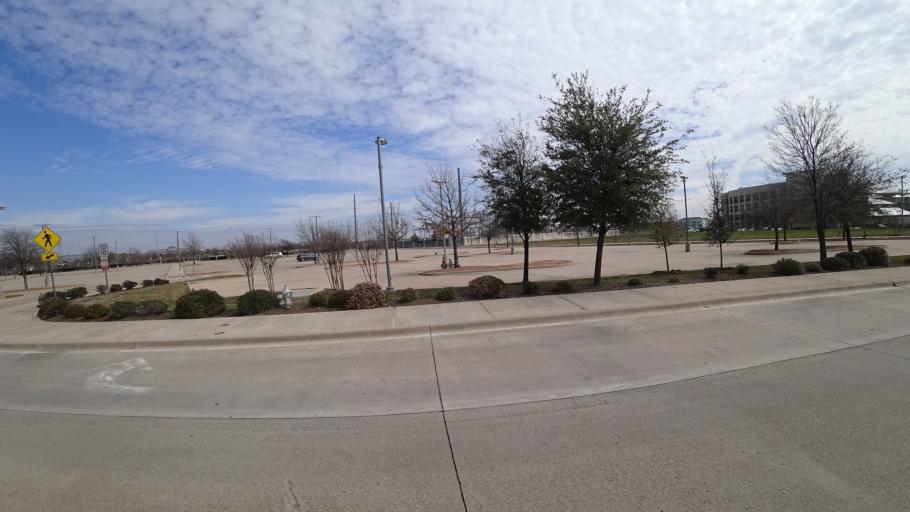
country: US
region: Texas
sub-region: Denton County
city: Lewisville
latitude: 33.0091
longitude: -96.9600
